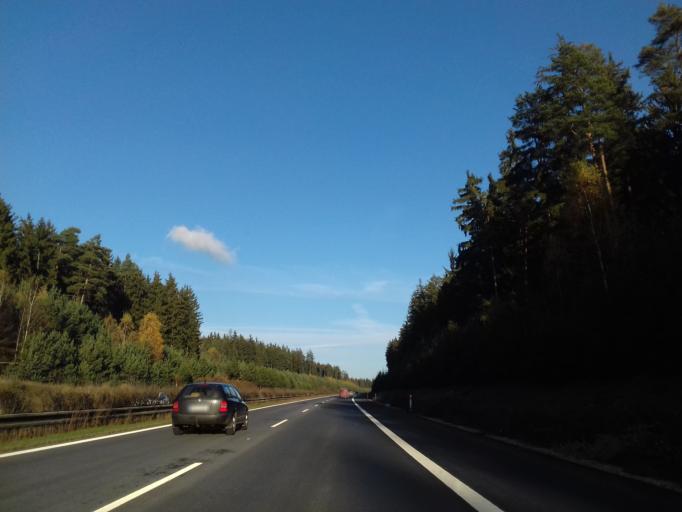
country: CZ
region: Plzensky
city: Holoubkov
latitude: 49.7708
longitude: 13.6547
